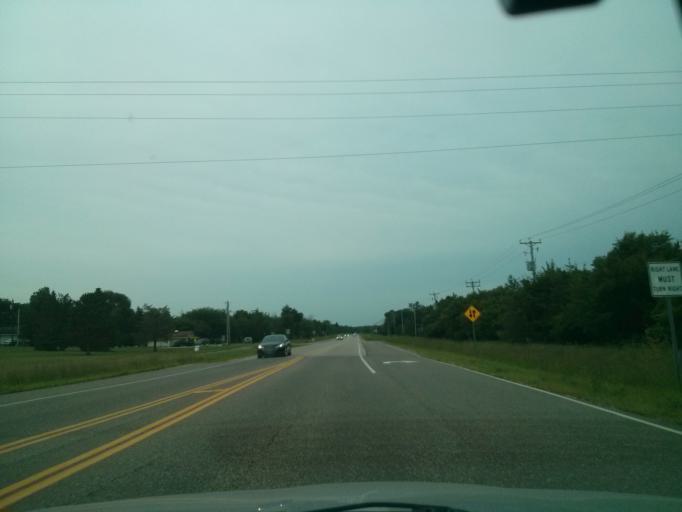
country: US
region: Minnesota
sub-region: Washington County
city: Lakeland
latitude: 44.9399
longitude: -92.7711
